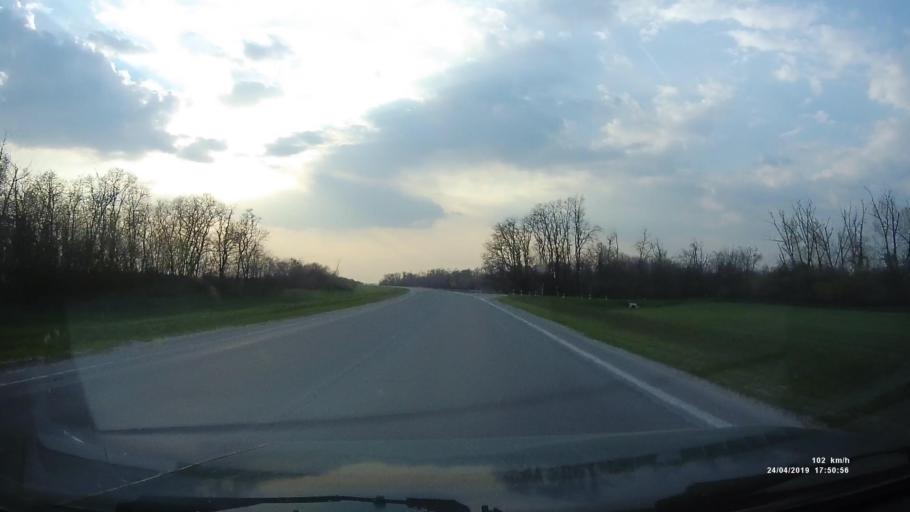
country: RU
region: Rostov
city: Yegorlykskaya
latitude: 46.5445
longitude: 40.7704
